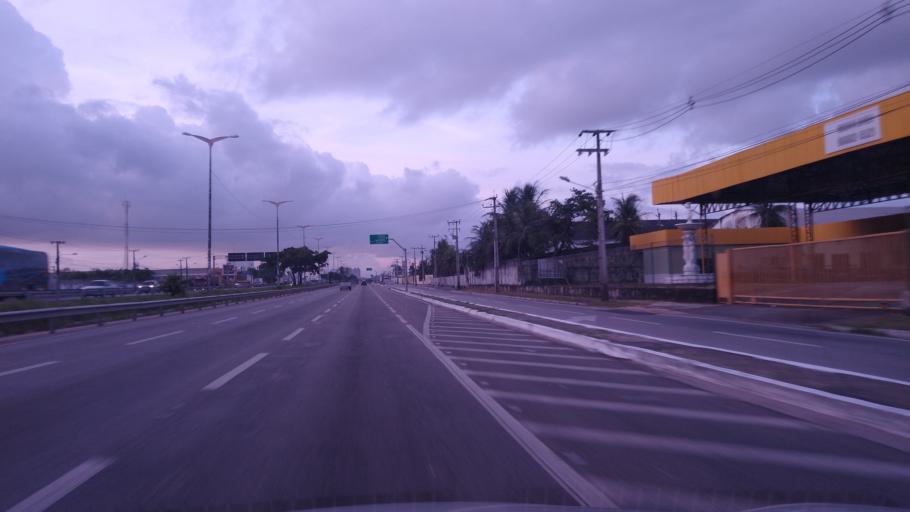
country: BR
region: Ceara
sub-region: Fortaleza
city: Fortaleza
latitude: -3.7856
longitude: -38.5120
